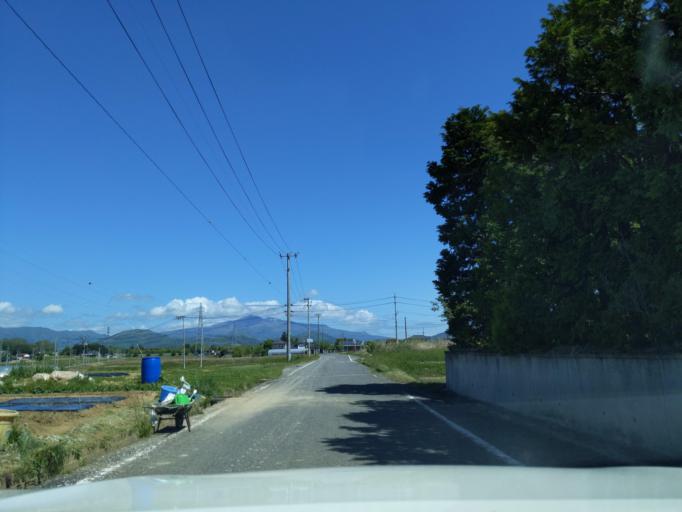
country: JP
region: Fukushima
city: Koriyama
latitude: 37.4407
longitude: 140.3276
